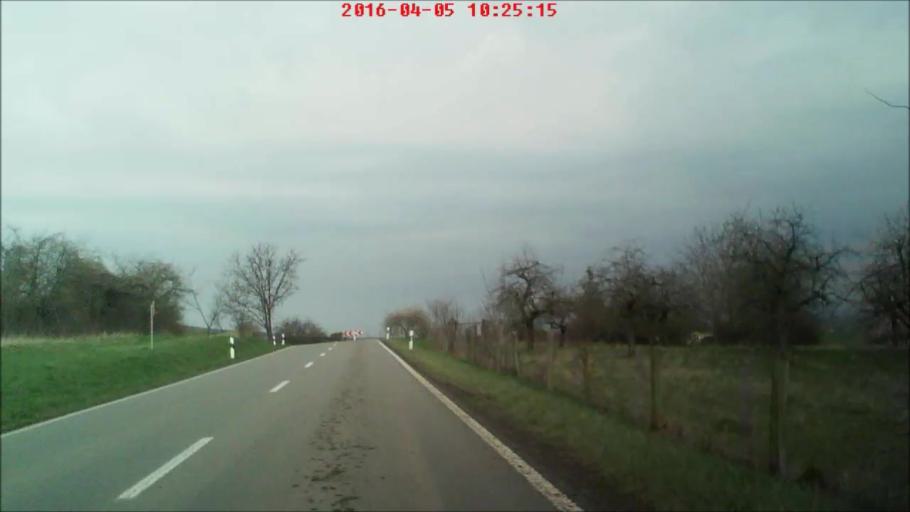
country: DE
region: Thuringia
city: Gierstadt
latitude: 51.0428
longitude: 10.8339
